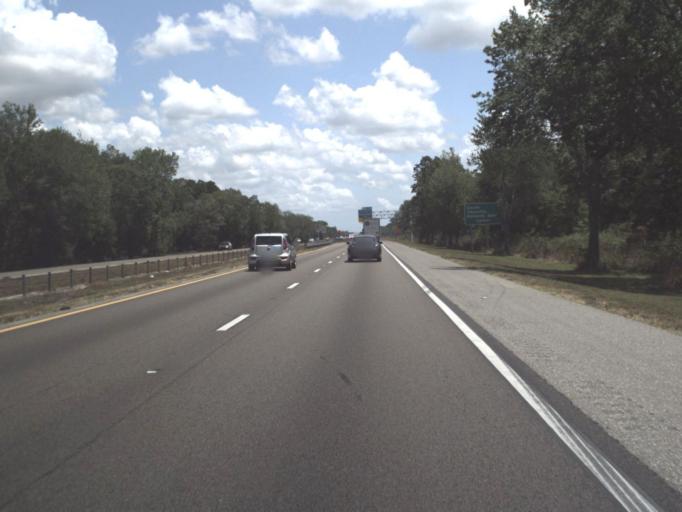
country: US
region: Florida
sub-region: Orange County
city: Wedgefield
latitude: 28.4514
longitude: -81.1212
